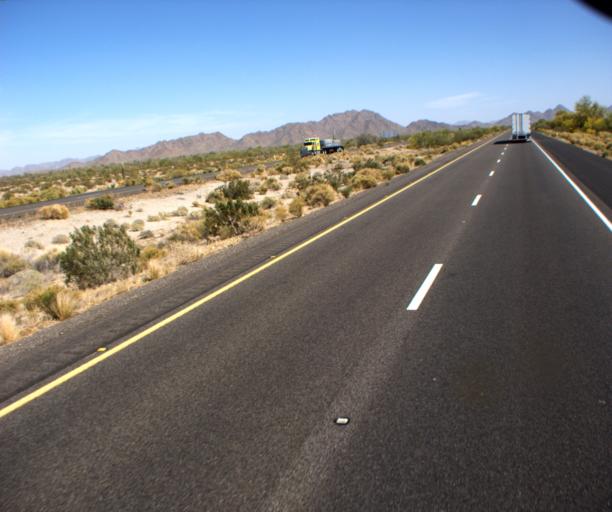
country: US
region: Arizona
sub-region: Maricopa County
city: Gila Bend
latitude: 32.9168
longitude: -112.6332
